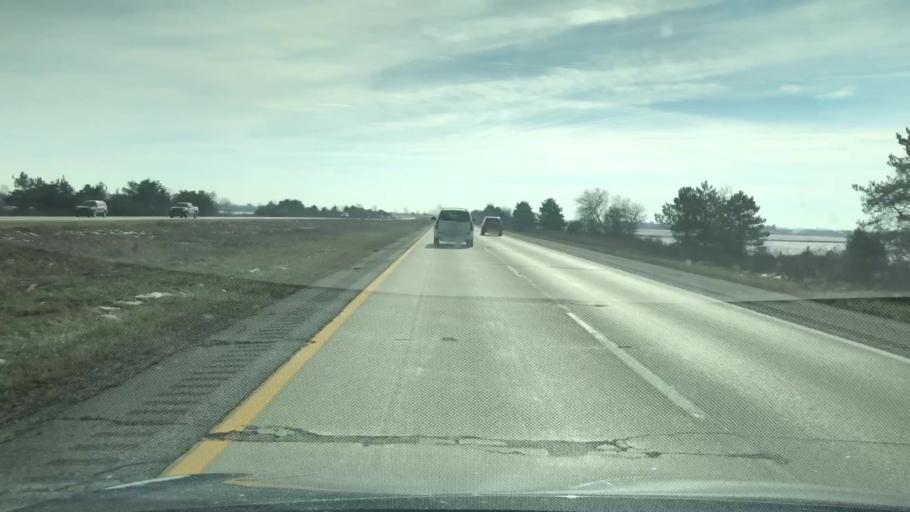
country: US
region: Michigan
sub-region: Bay County
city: Auburn
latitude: 43.6797
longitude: -84.0133
